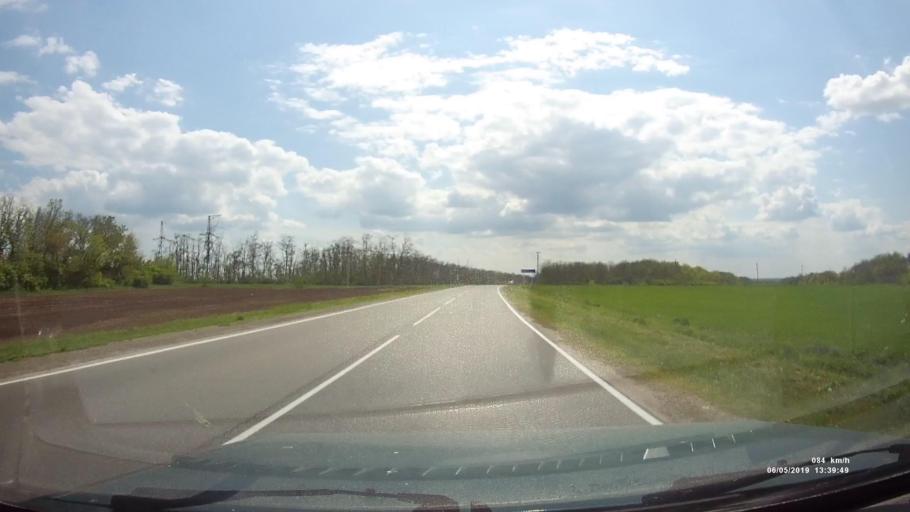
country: RU
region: Rostov
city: Ust'-Donetskiy
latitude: 47.6715
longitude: 40.7013
